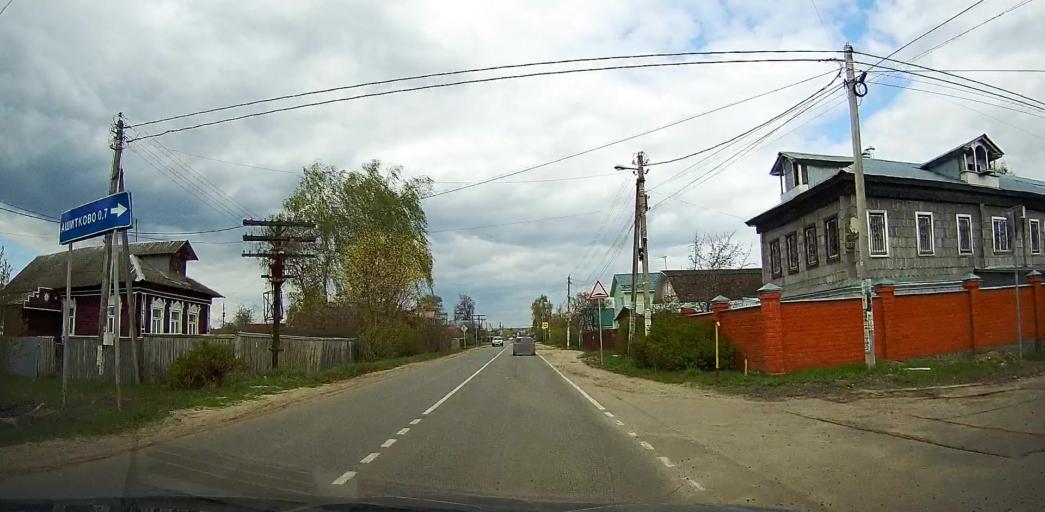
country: RU
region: Moskovskaya
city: Ashitkovo
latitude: 55.4466
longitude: 38.5918
